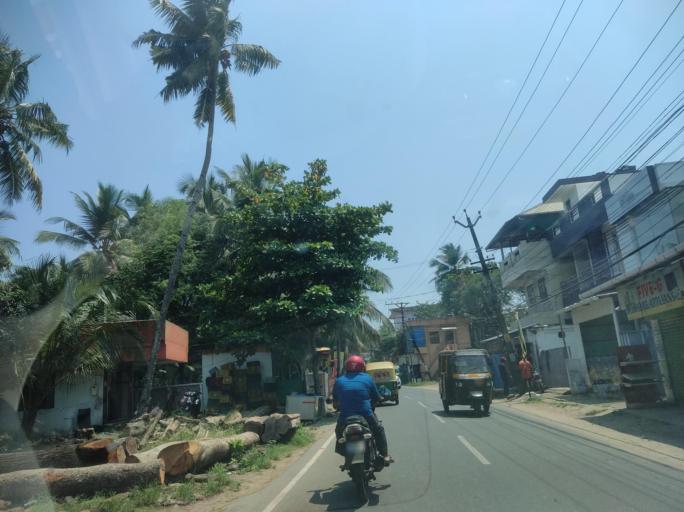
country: IN
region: Kerala
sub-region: Ernakulam
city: Cochin
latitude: 9.8893
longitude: 76.2855
